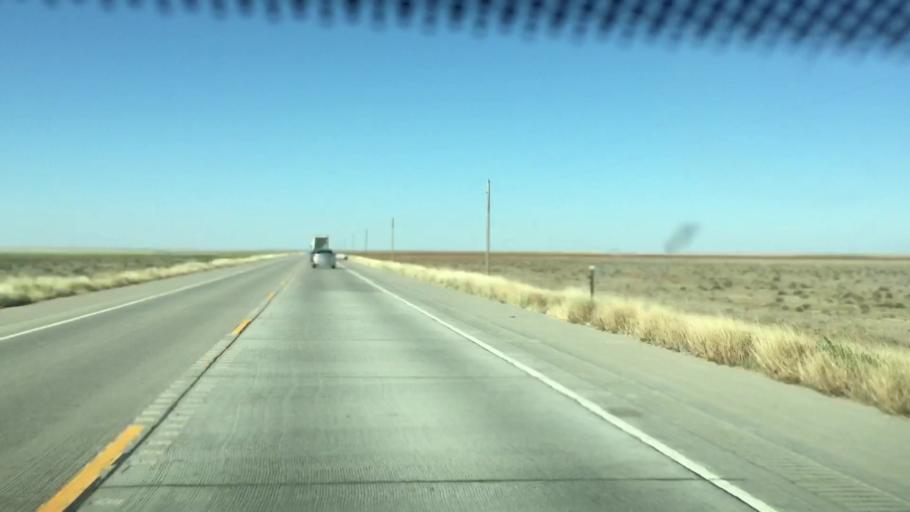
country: US
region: Colorado
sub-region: Kiowa County
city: Eads
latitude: 38.2842
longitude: -102.7199
